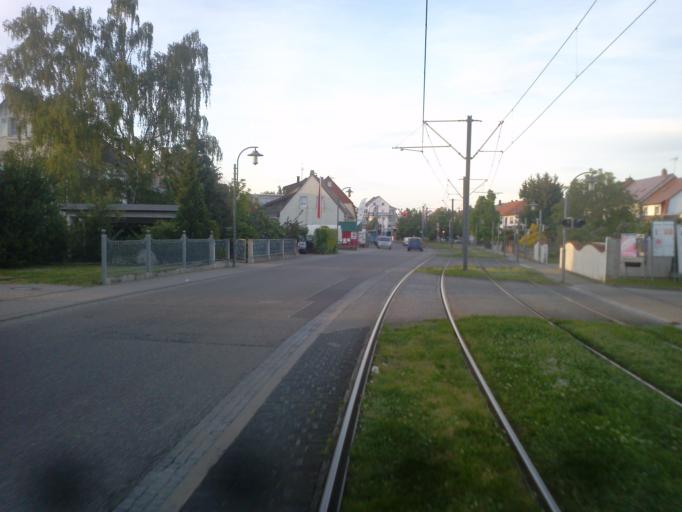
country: DE
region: Baden-Wuerttemberg
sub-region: Karlsruhe Region
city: Weingarten
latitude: 49.0590
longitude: 8.4683
